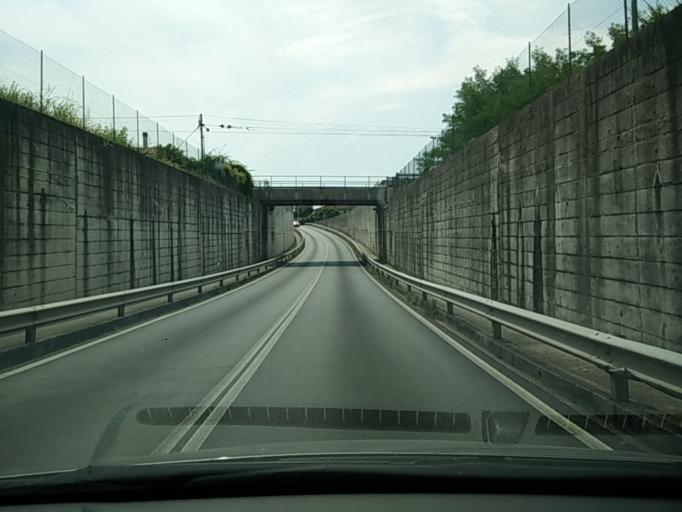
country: IT
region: Veneto
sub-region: Provincia di Treviso
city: San Floriano-Olmi
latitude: 45.6785
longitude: 12.3302
